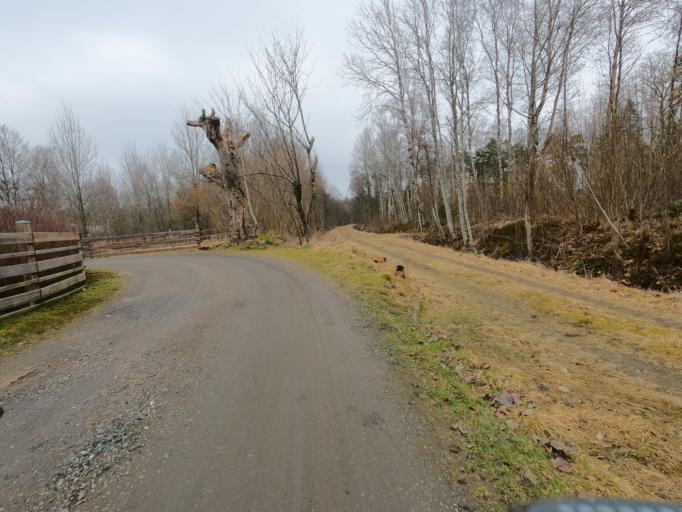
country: SE
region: Kronoberg
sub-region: Ljungby Kommun
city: Ljungby
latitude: 56.8183
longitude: 13.7025
